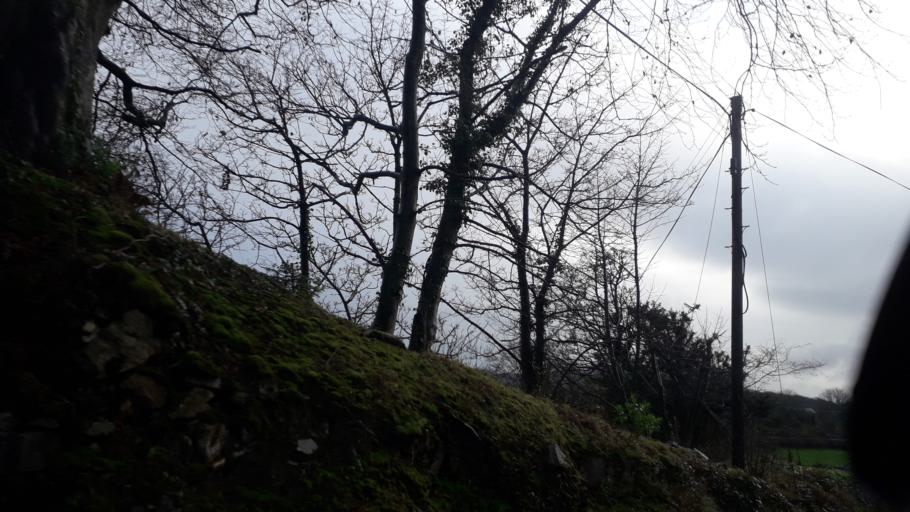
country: IE
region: Ulster
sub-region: County Donegal
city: Buncrana
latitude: 55.1151
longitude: -7.5316
